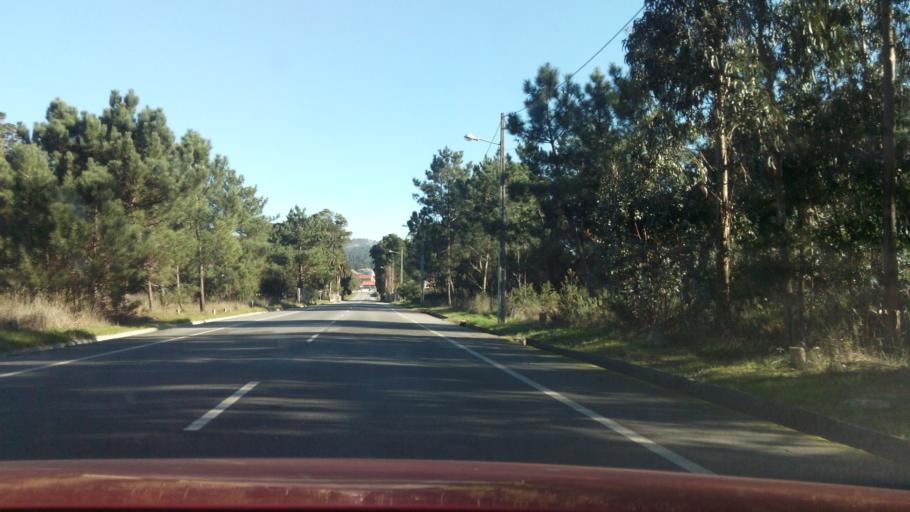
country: ES
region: Galicia
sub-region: Provincia de Pontevedra
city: O Grove
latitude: 42.4681
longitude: -8.9145
